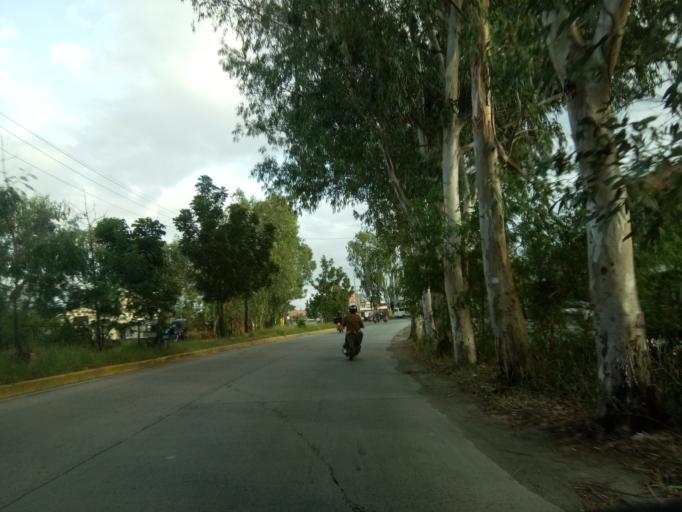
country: PH
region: Calabarzon
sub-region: Province of Cavite
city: Imus
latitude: 14.3883
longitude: 120.9699
